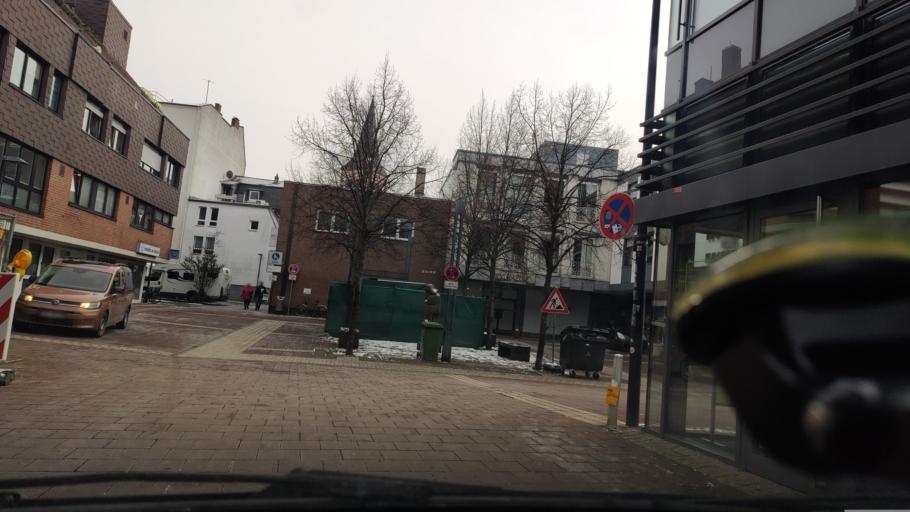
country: DE
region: North Rhine-Westphalia
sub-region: Regierungsbezirk Koln
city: Siegburg
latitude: 50.7974
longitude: 7.2058
